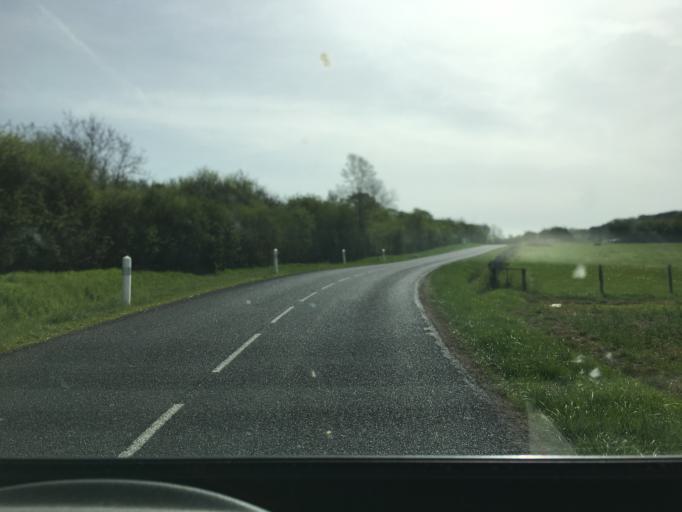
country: FR
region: Lorraine
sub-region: Departement de Meurthe-et-Moselle
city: Dommartin-les-Toul
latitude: 48.6705
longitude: 5.9356
